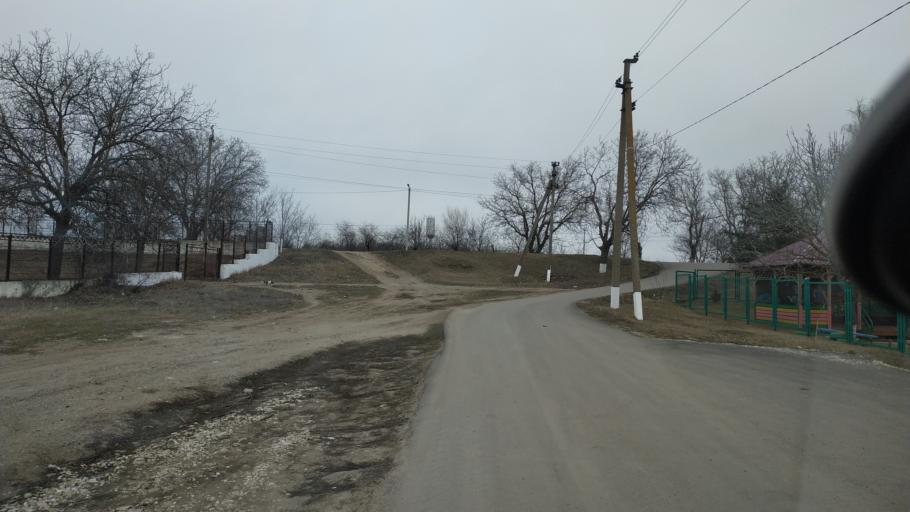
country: MD
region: Telenesti
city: Cocieri
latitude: 47.3543
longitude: 29.1158
